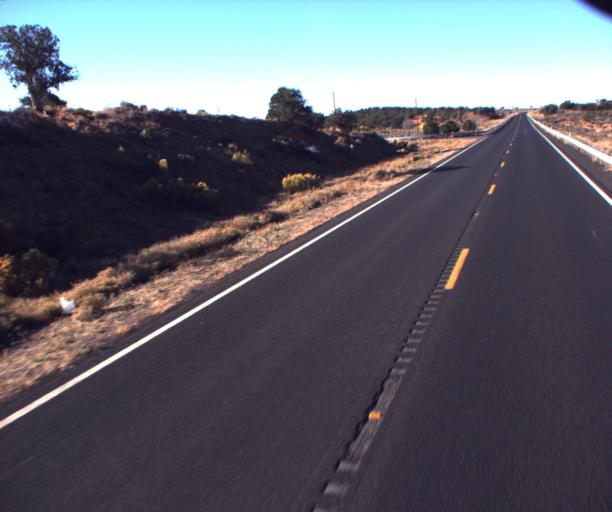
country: US
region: Arizona
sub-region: Apache County
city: Ganado
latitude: 35.7645
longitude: -109.7499
